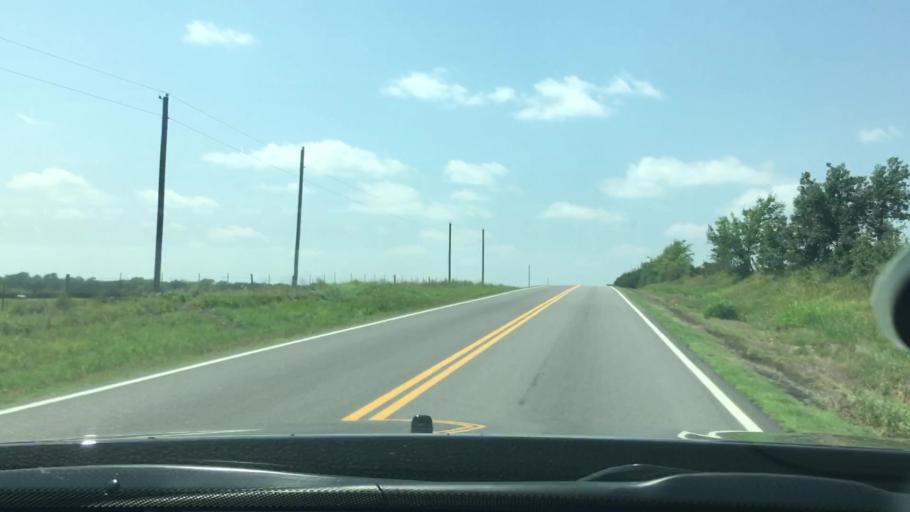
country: US
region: Oklahoma
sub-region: Atoka County
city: Atoka
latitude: 34.3750
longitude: -96.2160
